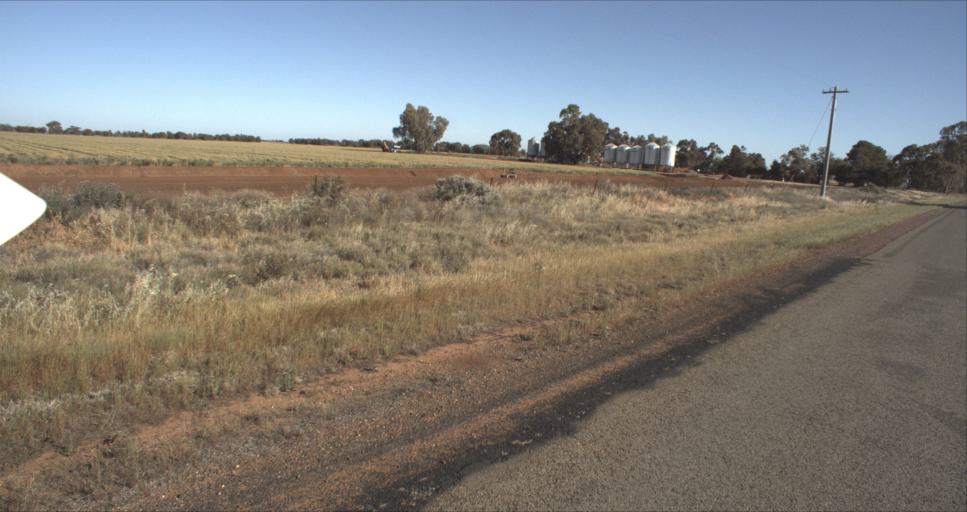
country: AU
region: New South Wales
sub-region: Leeton
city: Leeton
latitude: -34.5574
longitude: 146.2661
